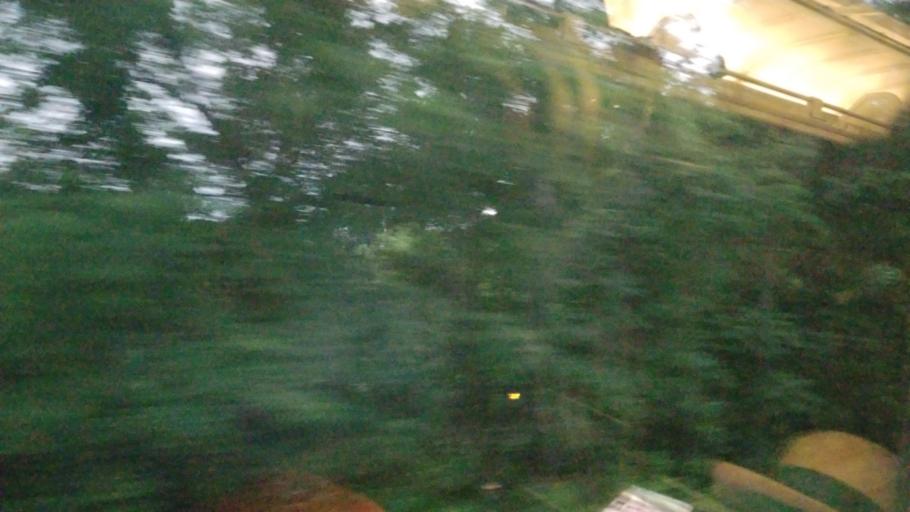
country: US
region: Virginia
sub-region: Orange County
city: Orange
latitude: 38.2414
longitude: -78.1147
